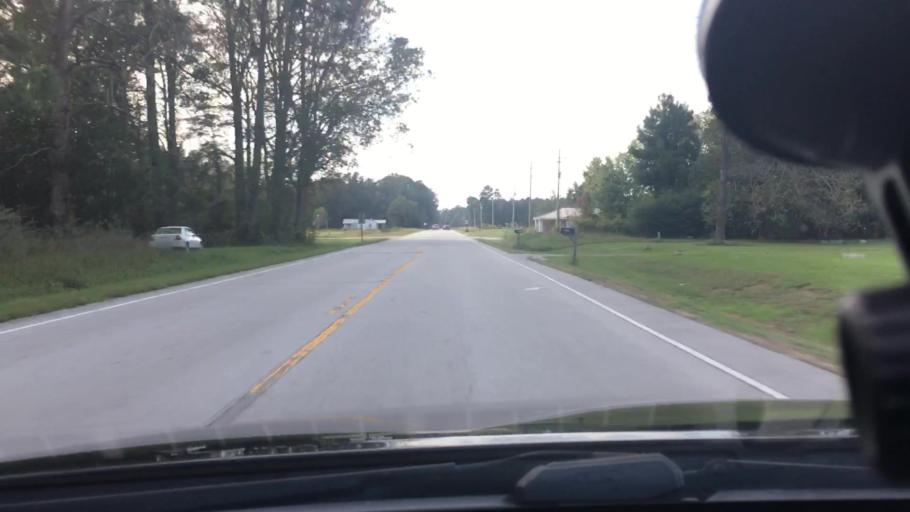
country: US
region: North Carolina
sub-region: Craven County
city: Vanceboro
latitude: 35.4000
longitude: -77.2375
